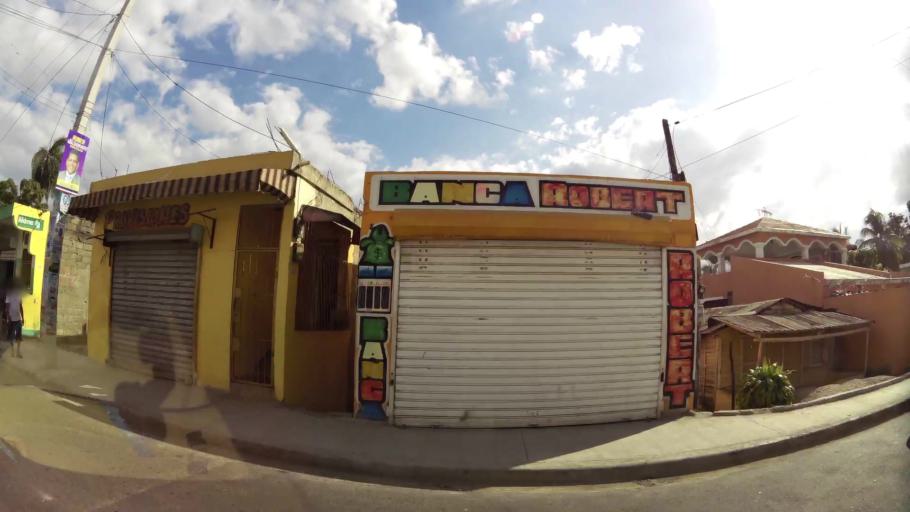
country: DO
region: Nacional
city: Ensanche Luperon
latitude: 18.5439
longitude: -69.8981
